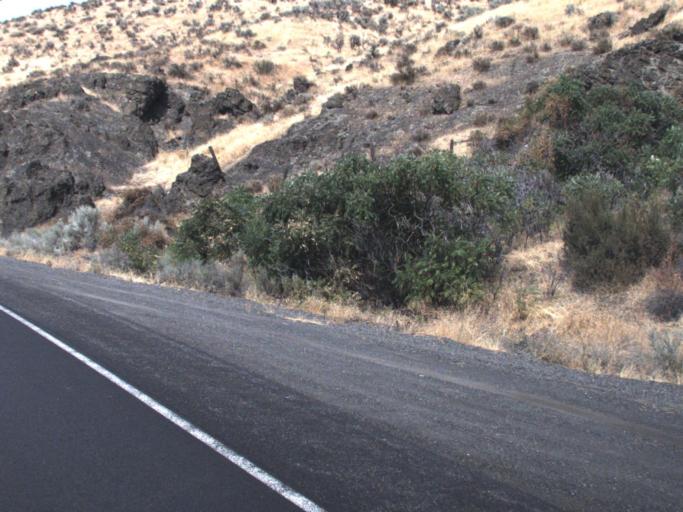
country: US
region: Washington
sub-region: Kittitas County
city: Kittitas
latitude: 46.8075
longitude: -120.4402
